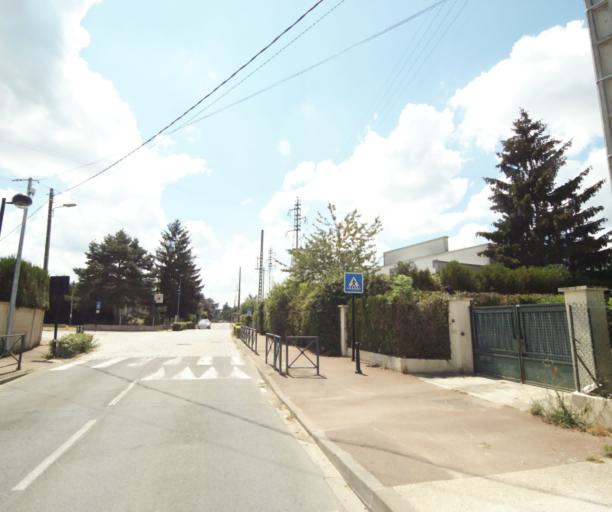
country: FR
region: Ile-de-France
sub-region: Departement de Seine-et-Marne
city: Samoreau
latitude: 48.4365
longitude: 2.7546
